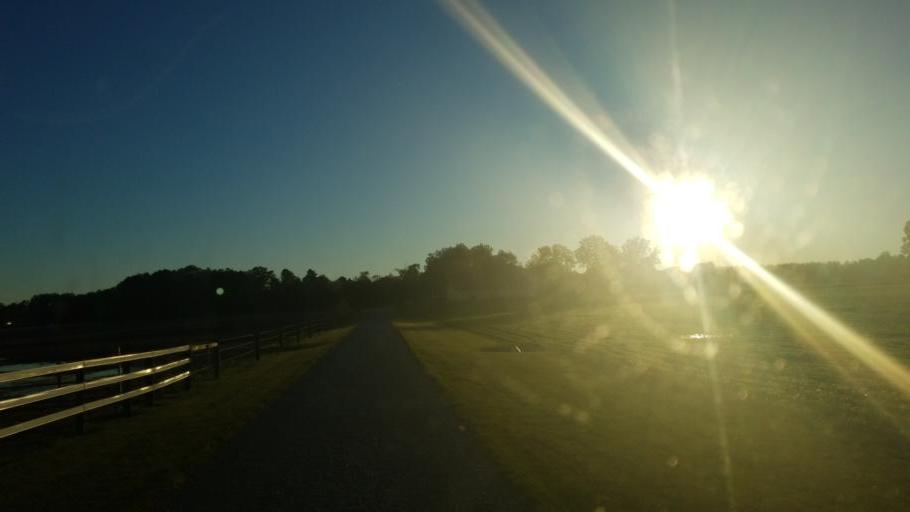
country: US
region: Indiana
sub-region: Elkhart County
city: Nappanee
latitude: 41.4681
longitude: -86.0418
